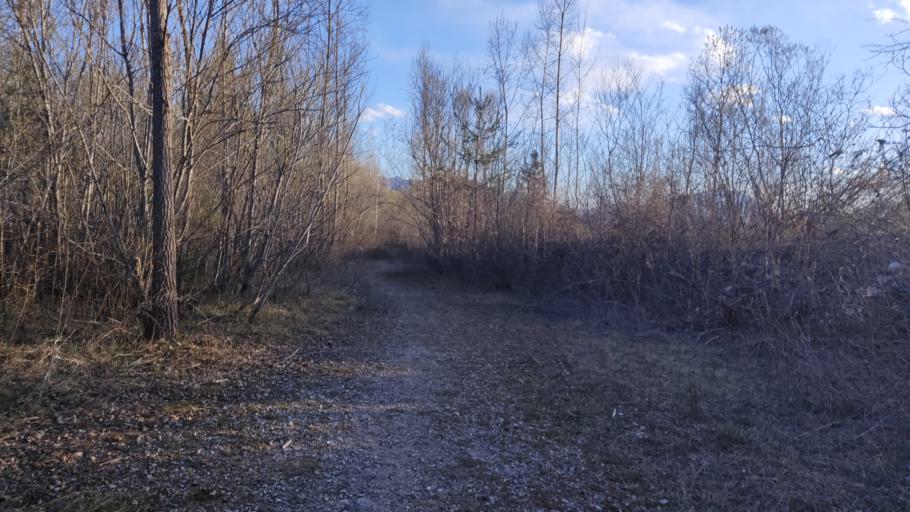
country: IT
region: Veneto
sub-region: Provincia di Belluno
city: Sedico
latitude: 46.1001
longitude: 12.0818
